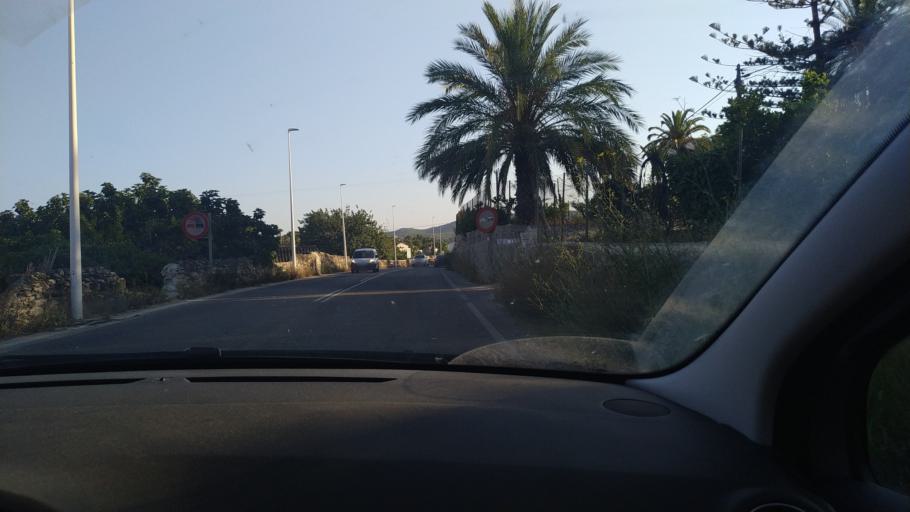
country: ES
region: Valencia
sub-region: Provincia de Alicante
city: Javea
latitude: 38.7826
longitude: 0.1563
